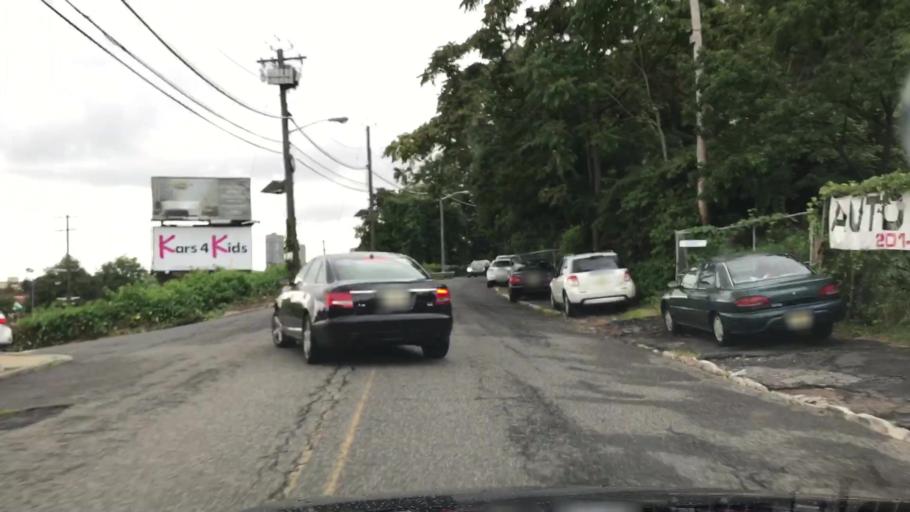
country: US
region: New Jersey
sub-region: Bergen County
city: Cliffside Park
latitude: 40.8143
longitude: -73.9845
